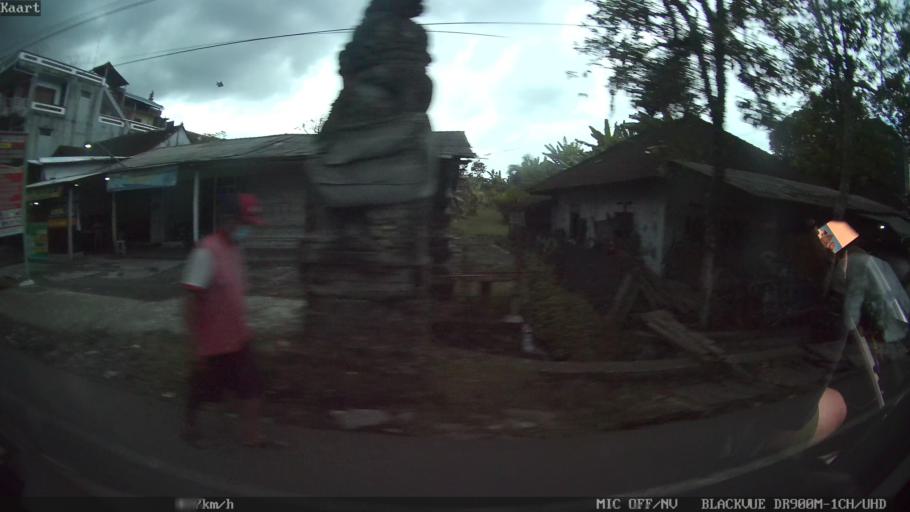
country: ID
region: Bali
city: Banjar Penyalin
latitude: -8.5338
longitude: 115.1092
